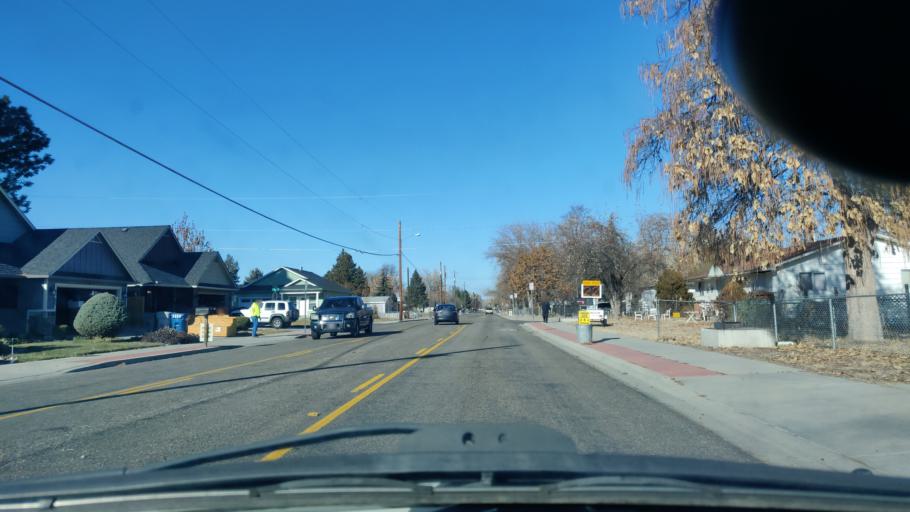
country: US
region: Idaho
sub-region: Ada County
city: Garden City
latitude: 43.6391
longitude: -116.2536
